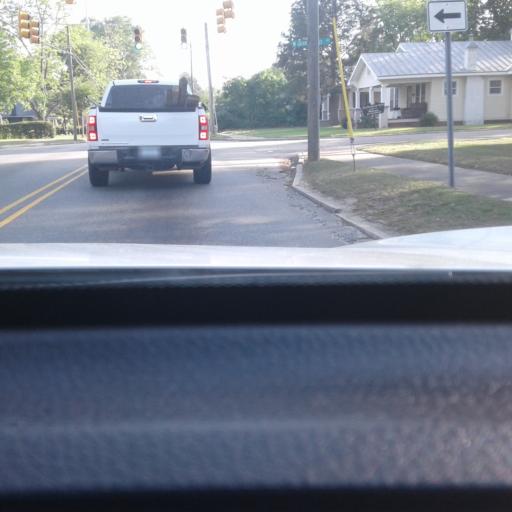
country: US
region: North Carolina
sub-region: Harnett County
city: Dunn
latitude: 35.3188
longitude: -78.6091
